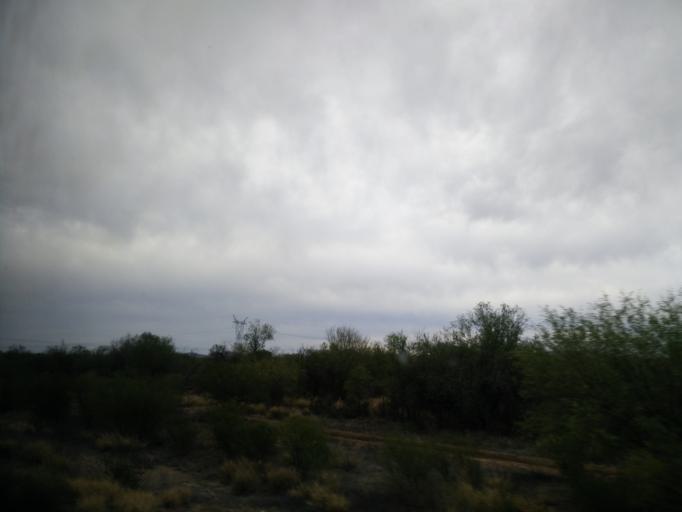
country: MX
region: Sonora
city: Hermosillo
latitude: 28.6623
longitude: -110.9997
